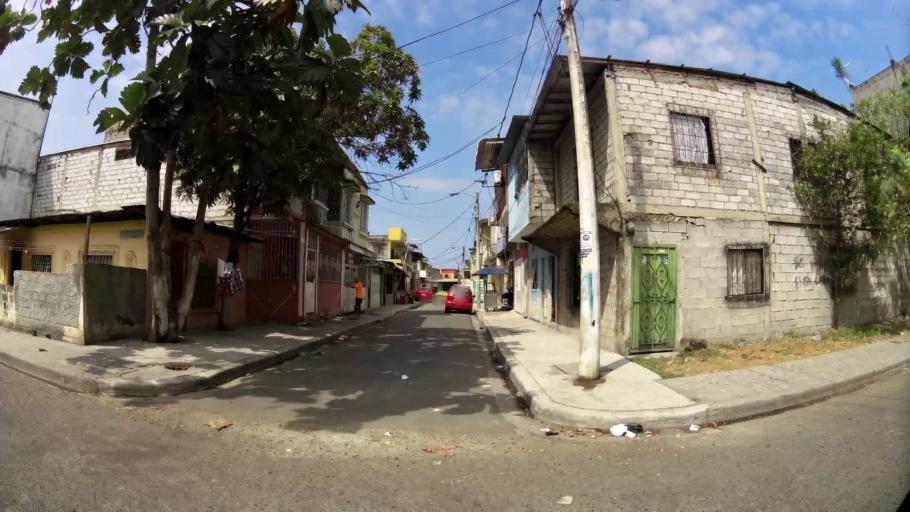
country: EC
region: Guayas
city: Guayaquil
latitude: -2.2543
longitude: -79.8905
